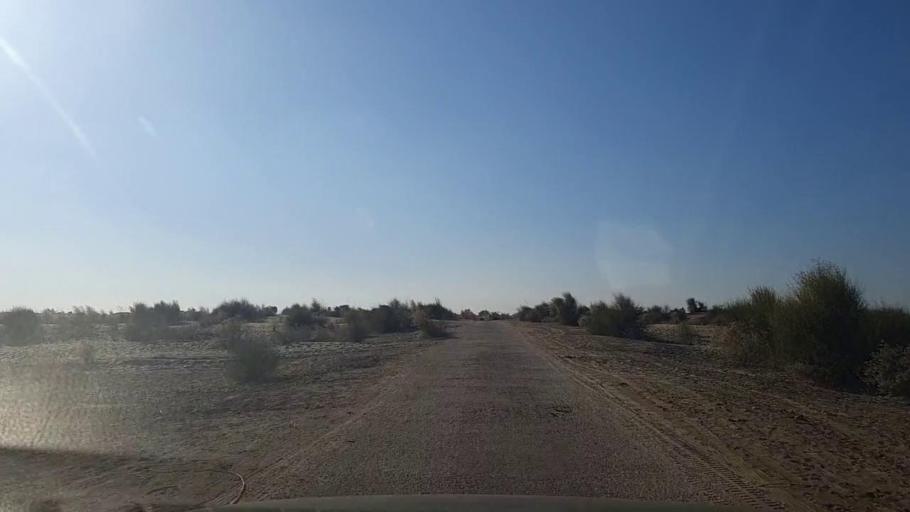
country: PK
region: Sindh
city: Khadro
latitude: 26.2413
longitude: 68.8825
